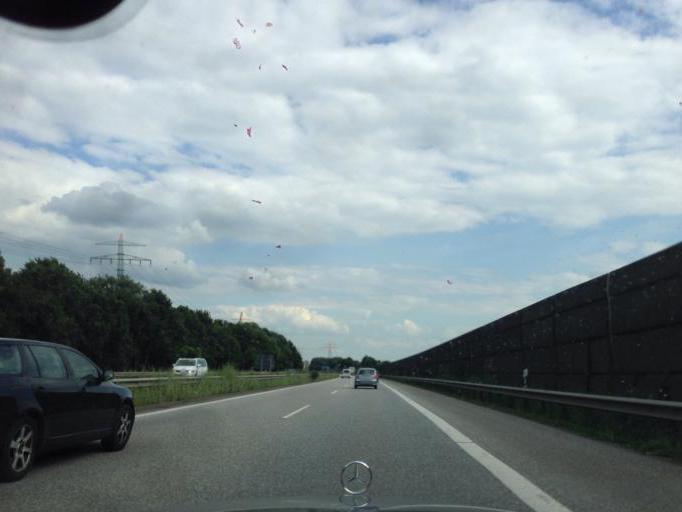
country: DE
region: Hamburg
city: Wandsbek
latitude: 53.4910
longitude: 10.1050
